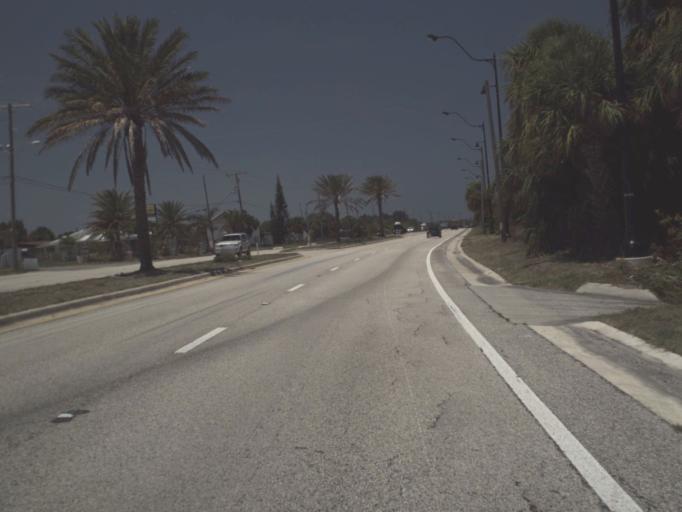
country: US
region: Florida
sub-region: Brevard County
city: Palm Bay
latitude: 28.0477
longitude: -80.5870
